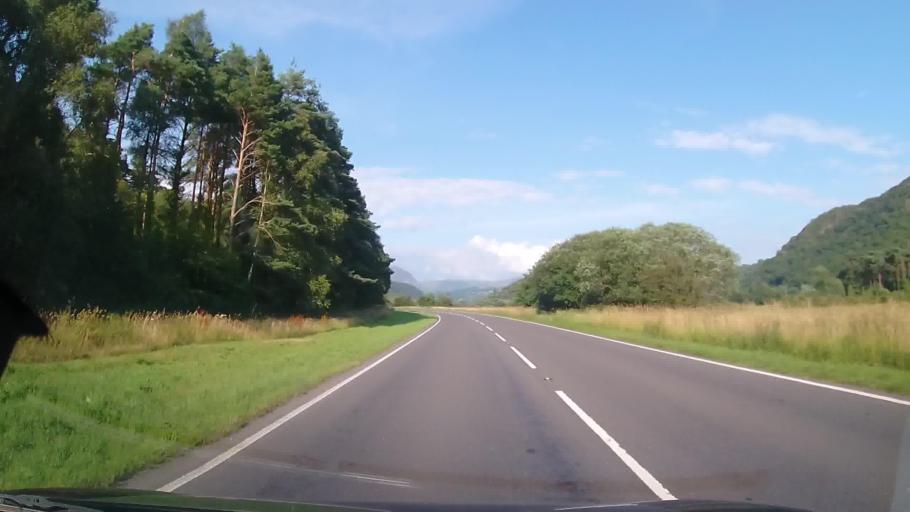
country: GB
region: Wales
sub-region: Gwynedd
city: Maentwrog
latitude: 52.9433
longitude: -4.0036
